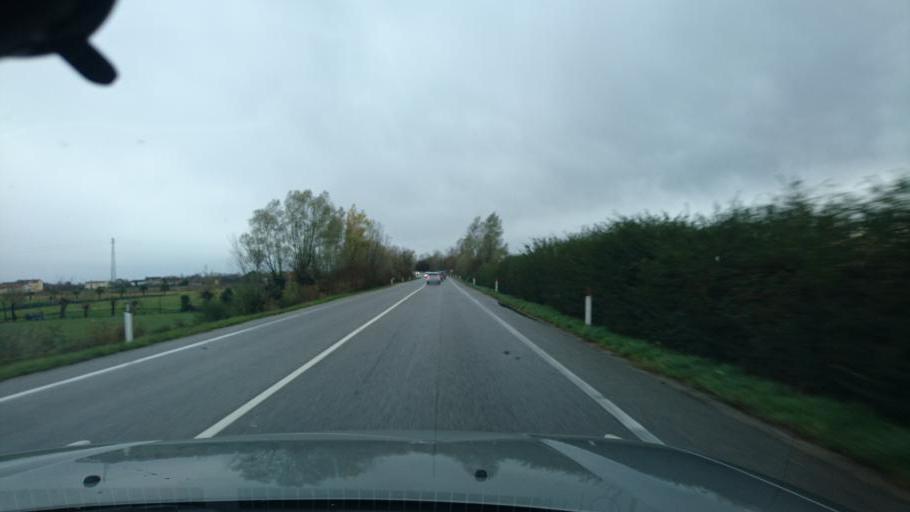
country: IT
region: Veneto
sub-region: Provincia di Padova
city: Campodarsego
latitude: 45.5031
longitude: 11.9300
